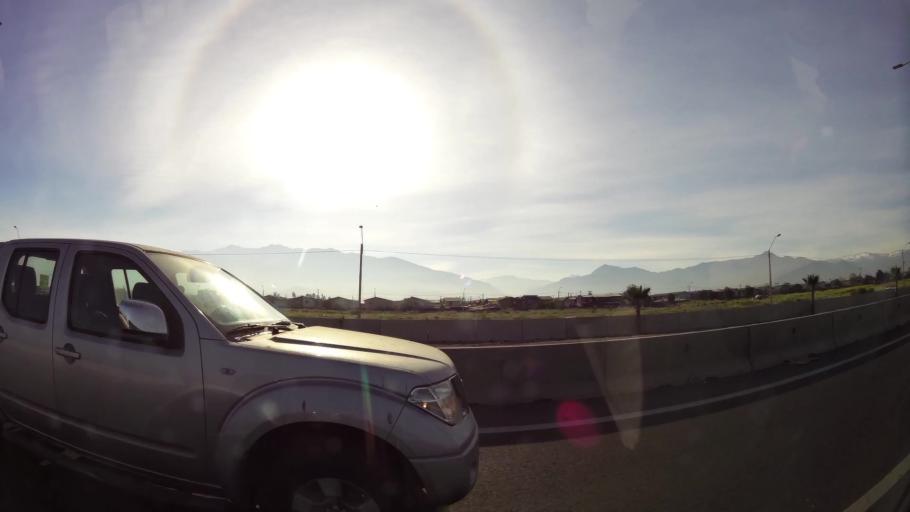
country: CL
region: Santiago Metropolitan
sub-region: Provincia de Santiago
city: La Pintana
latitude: -33.5718
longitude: -70.6125
